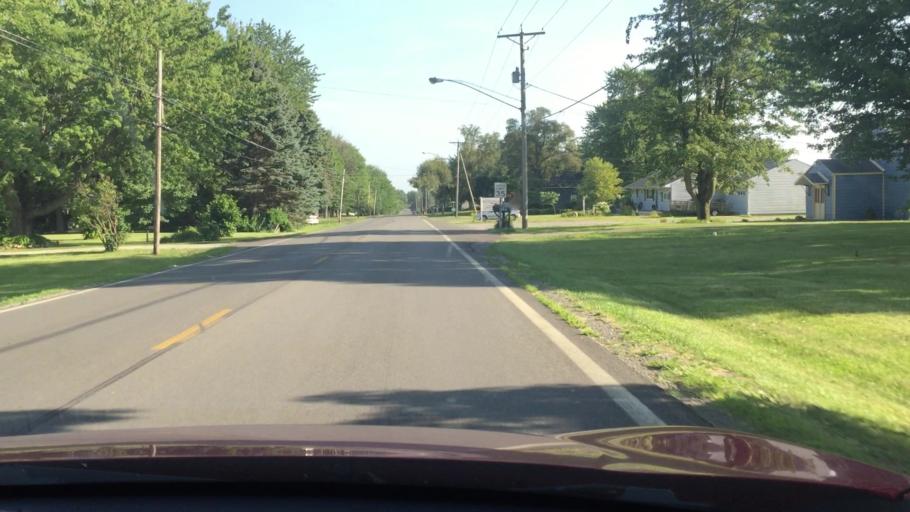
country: US
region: Ohio
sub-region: Hardin County
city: Ada
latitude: 40.7165
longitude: -83.8422
